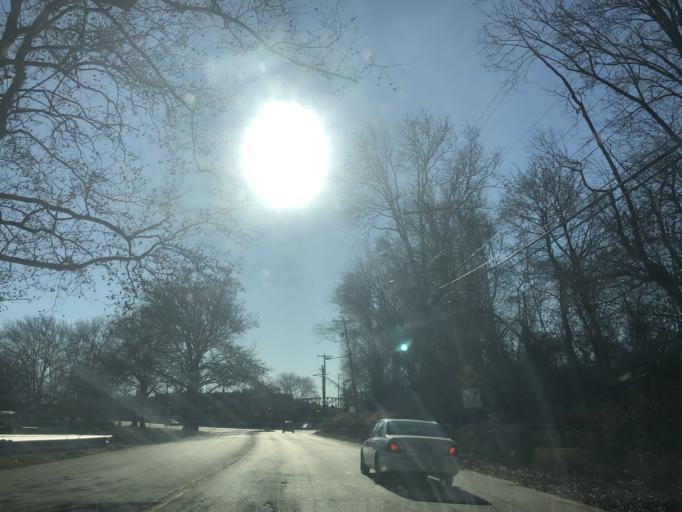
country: US
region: Pennsylvania
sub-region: Montgomery County
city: Bala-Cynwyd
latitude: 39.9839
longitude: -75.2270
